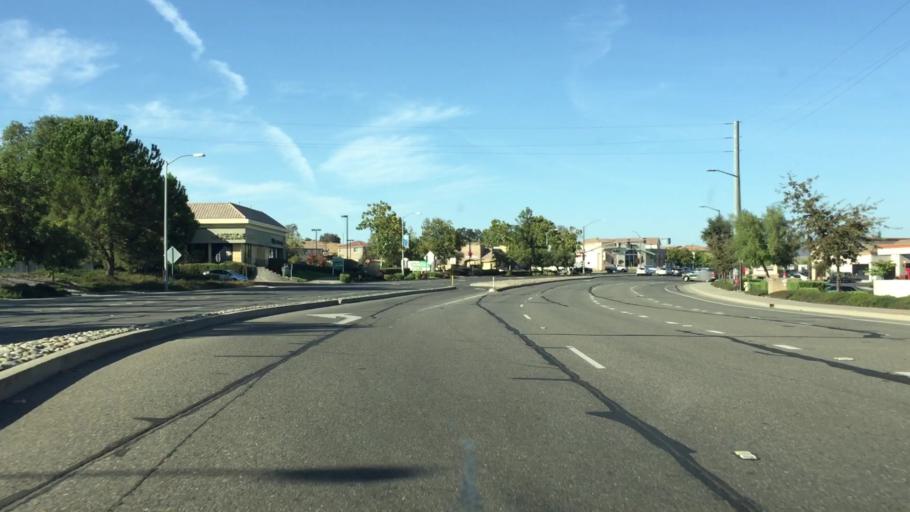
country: US
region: California
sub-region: El Dorado County
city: El Dorado Hills
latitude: 38.6890
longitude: -121.1238
